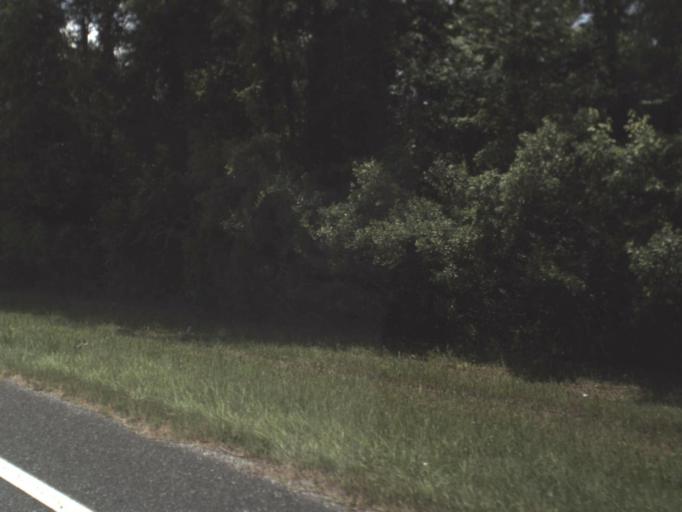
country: US
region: Florida
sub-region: Dixie County
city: Cross City
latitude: 29.6532
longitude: -83.1742
